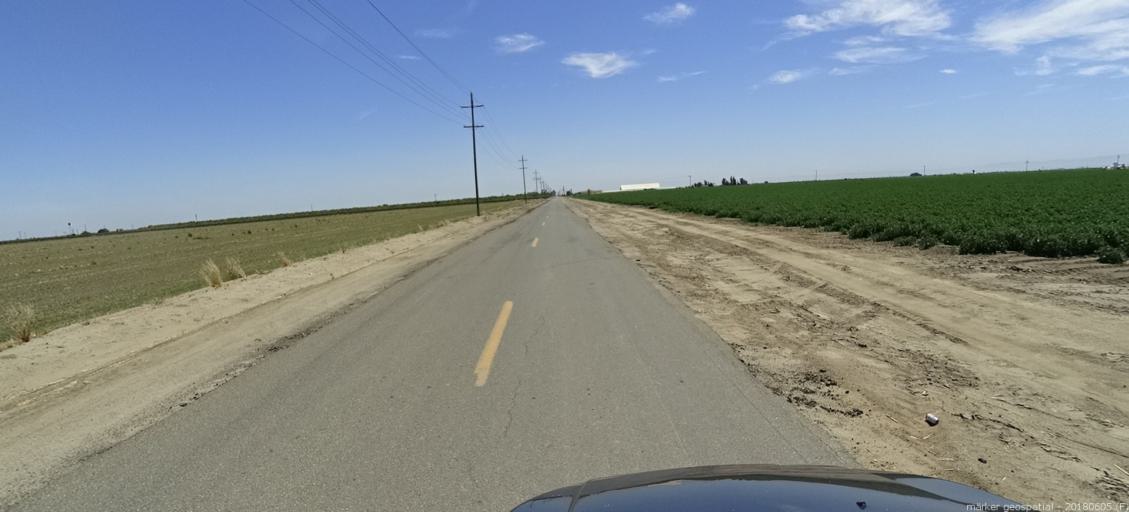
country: US
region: California
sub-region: Merced County
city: Dos Palos
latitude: 37.0949
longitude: -120.4735
